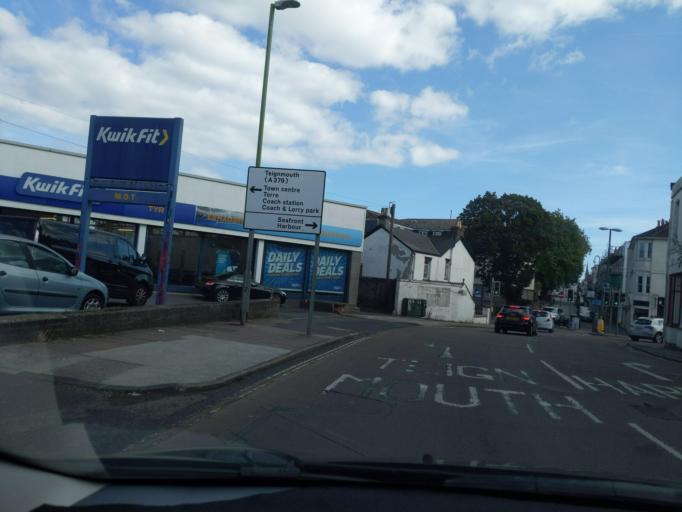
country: GB
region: England
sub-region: Borough of Torbay
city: Torquay
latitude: 50.4714
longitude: -3.5404
